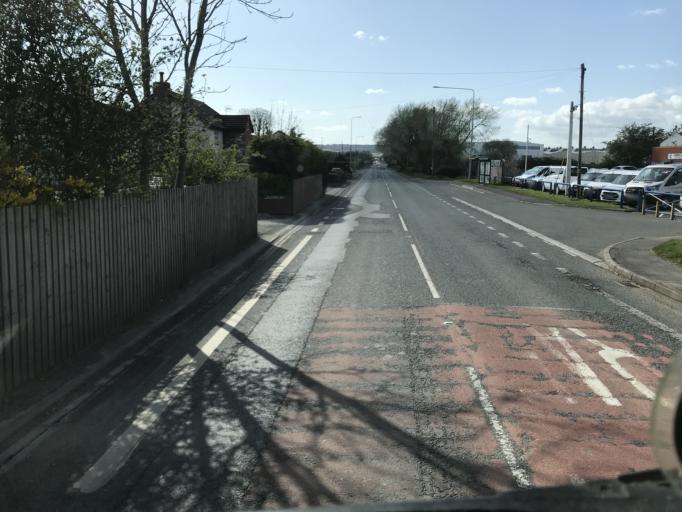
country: GB
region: England
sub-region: Cheshire West and Chester
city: Blacon
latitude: 53.1730
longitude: -2.9621
